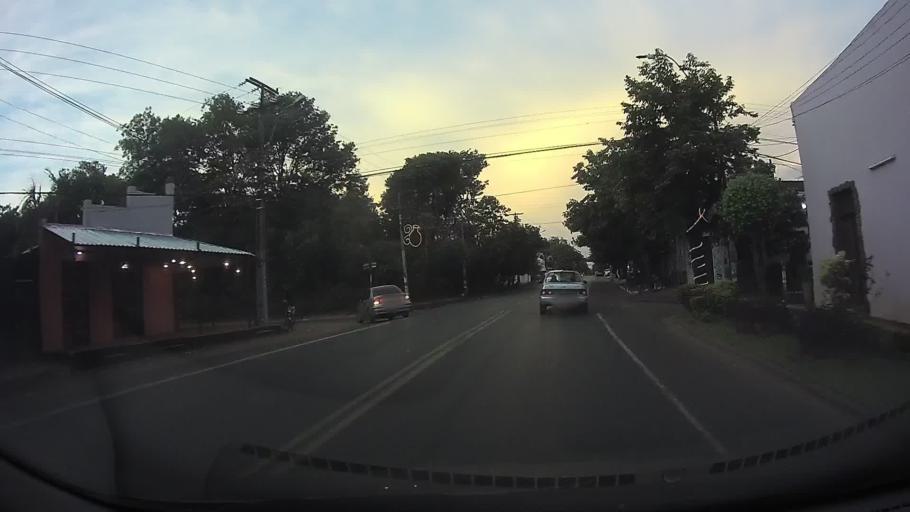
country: PY
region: Central
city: Ita
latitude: -25.5103
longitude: -57.3569
